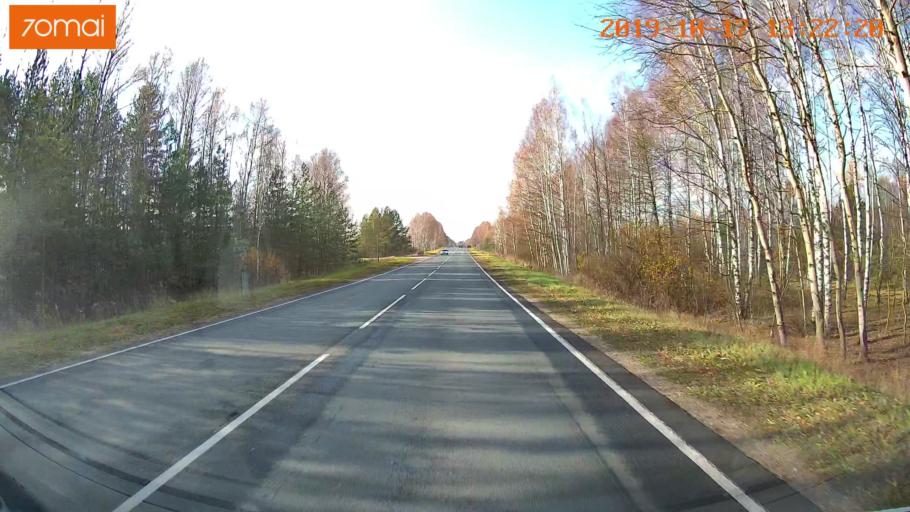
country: RU
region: Rjazan
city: Gus'-Zheleznyy
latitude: 55.0856
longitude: 41.0059
